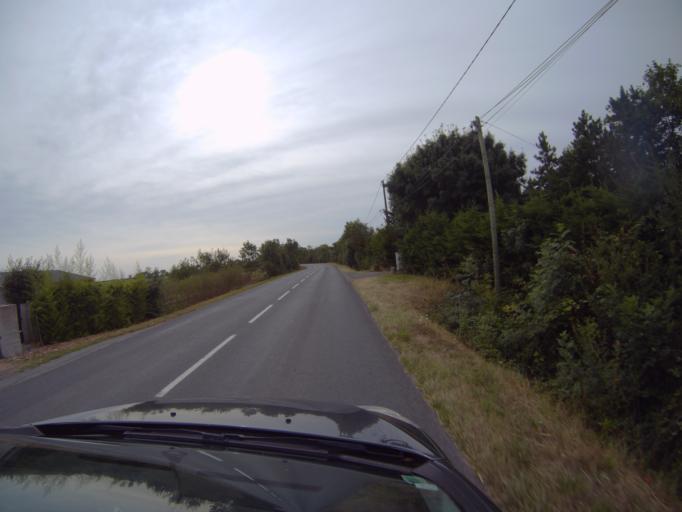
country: FR
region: Pays de la Loire
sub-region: Departement de la Vendee
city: Triaize
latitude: 46.3877
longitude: -1.1833
